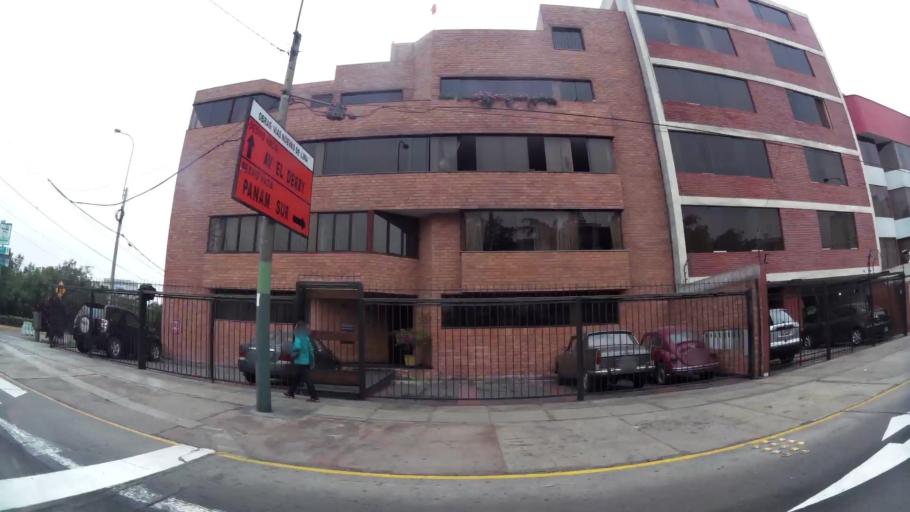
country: PE
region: Lima
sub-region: Lima
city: San Luis
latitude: -12.0961
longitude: -76.9894
